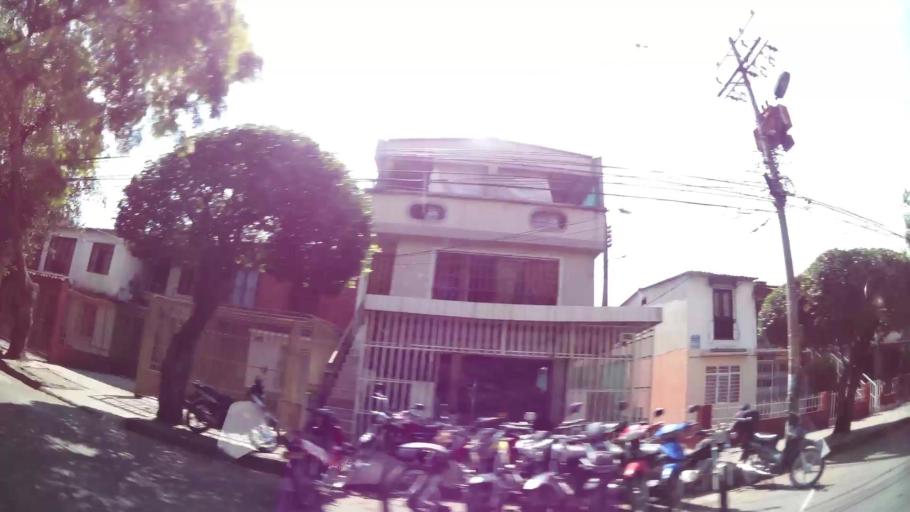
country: CO
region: Valle del Cauca
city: Cali
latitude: 3.4930
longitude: -76.4994
